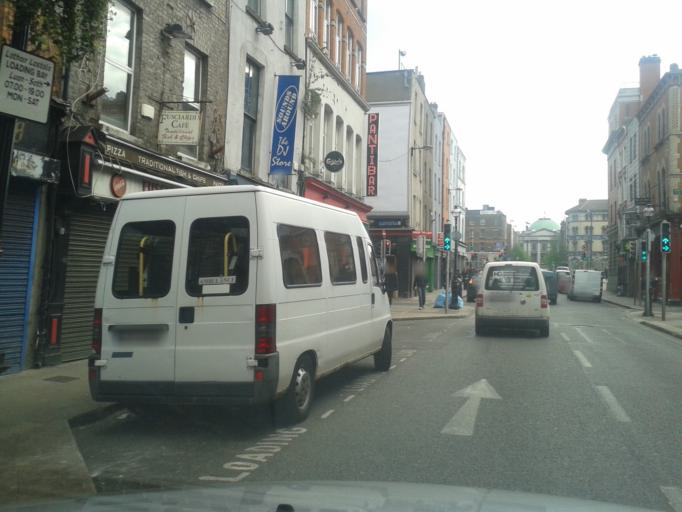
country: IE
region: Leinster
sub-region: Dublin City
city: Dublin
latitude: 53.3468
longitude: -6.2681
